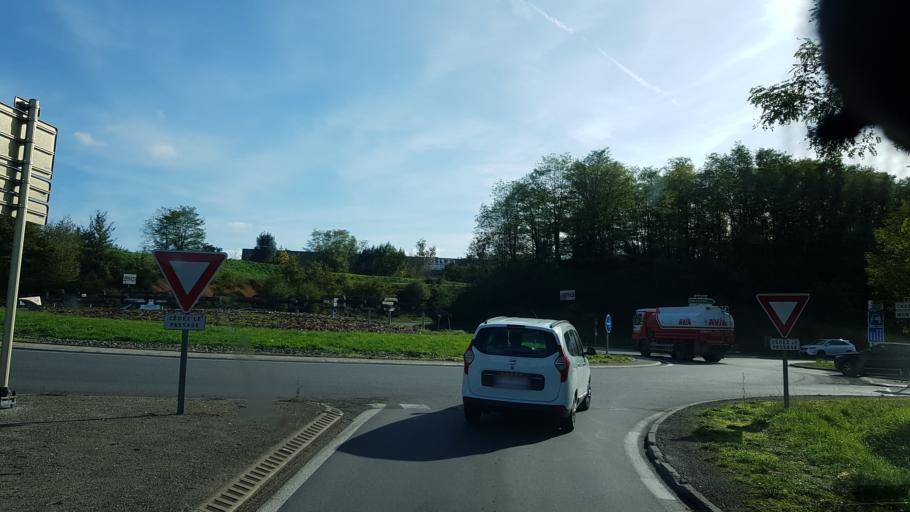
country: FR
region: Poitou-Charentes
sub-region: Departement de la Charente
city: Chasseneuil-sur-Bonnieure
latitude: 45.8325
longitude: 0.4688
